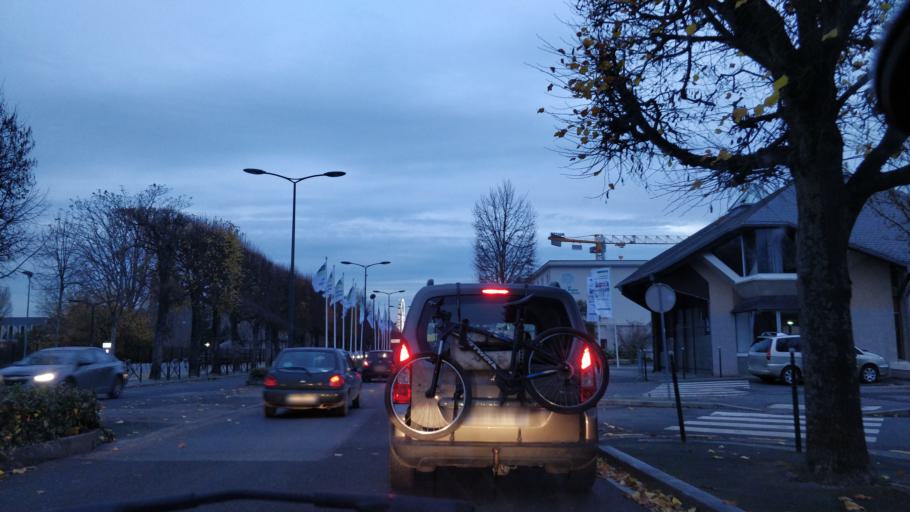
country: FR
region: Lower Normandy
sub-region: Departement du Calvados
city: Caen
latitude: 49.1768
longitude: -0.3710
